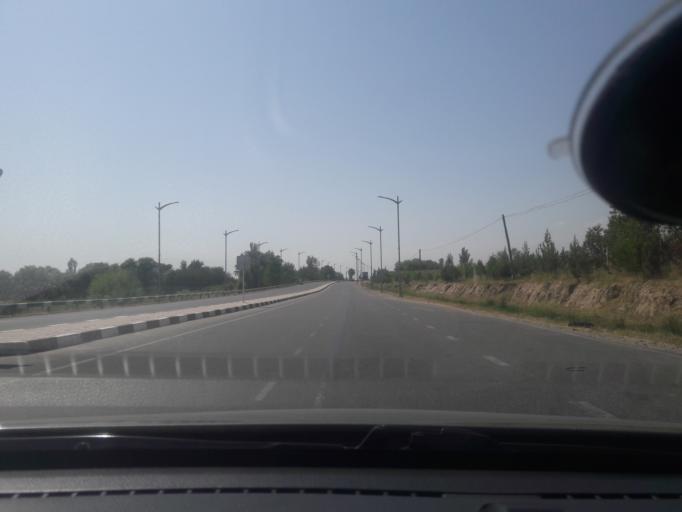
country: TJ
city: Shahrinav
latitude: 38.5641
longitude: 68.4079
